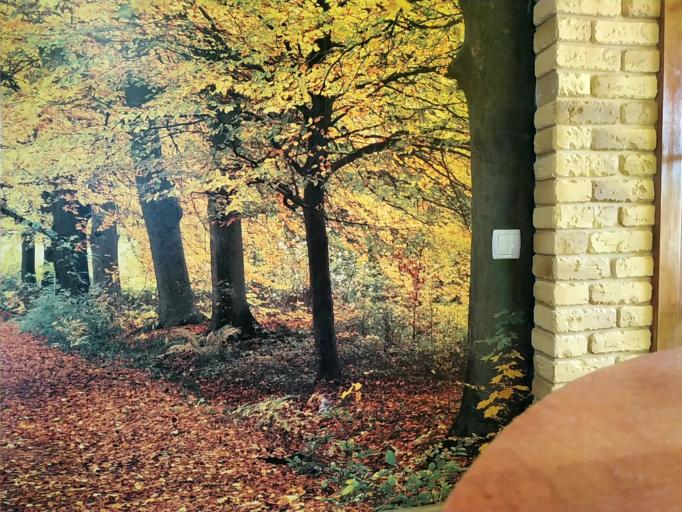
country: RU
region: Pskov
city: Dno
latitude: 57.9109
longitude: 30.1787
